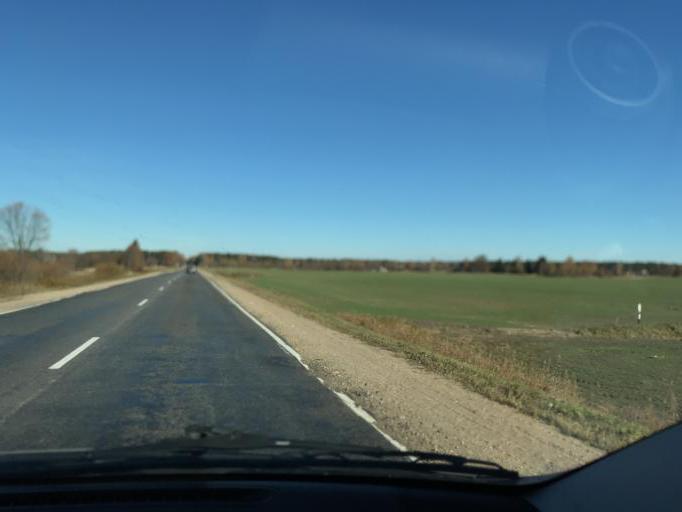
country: BY
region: Vitebsk
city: Lyepyel'
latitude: 55.0506
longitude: 28.7509
